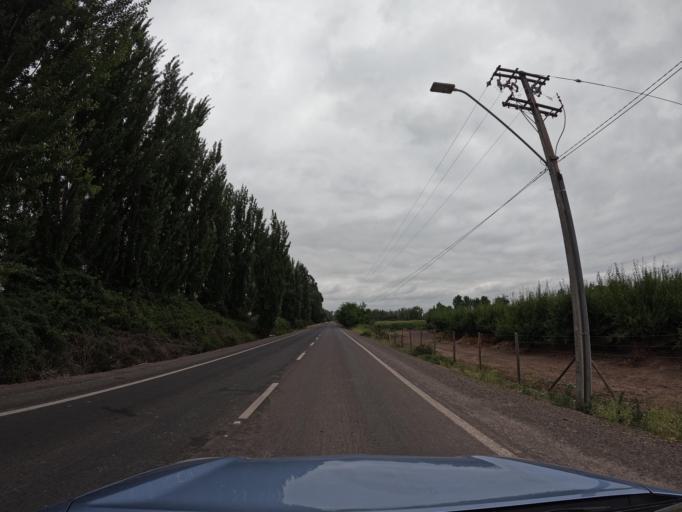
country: CL
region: O'Higgins
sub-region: Provincia de Colchagua
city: Chimbarongo
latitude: -34.7299
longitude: -71.0762
